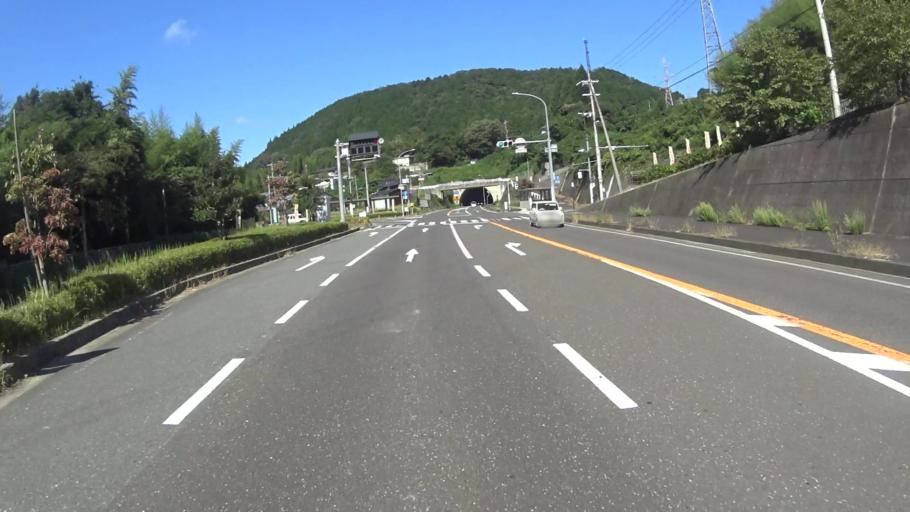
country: JP
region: Kyoto
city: Ayabe
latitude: 35.2606
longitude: 135.4082
